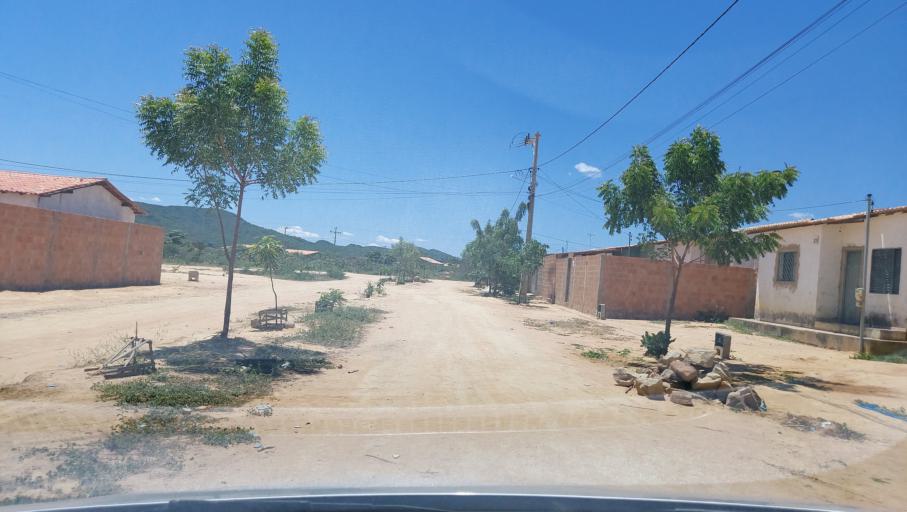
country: BR
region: Bahia
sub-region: Oliveira Dos Brejinhos
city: Beira Rio
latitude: -12.0034
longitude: -42.6337
